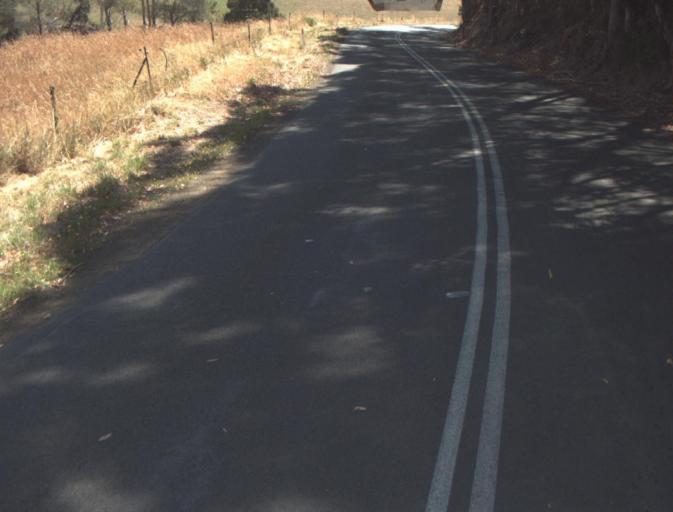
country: AU
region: Tasmania
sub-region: Launceston
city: Mayfield
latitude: -41.2683
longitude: 147.1290
